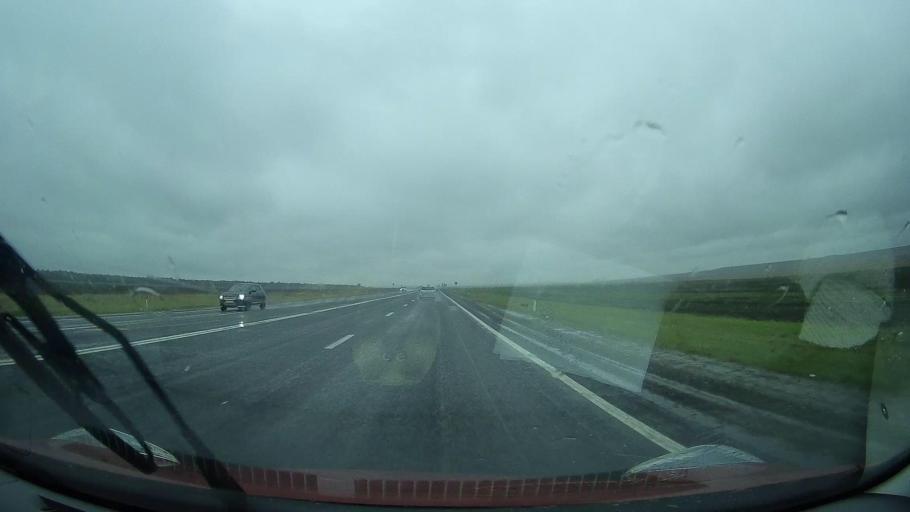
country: RU
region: Stavropol'skiy
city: Nevinnomyssk
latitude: 44.6262
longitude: 42.0548
